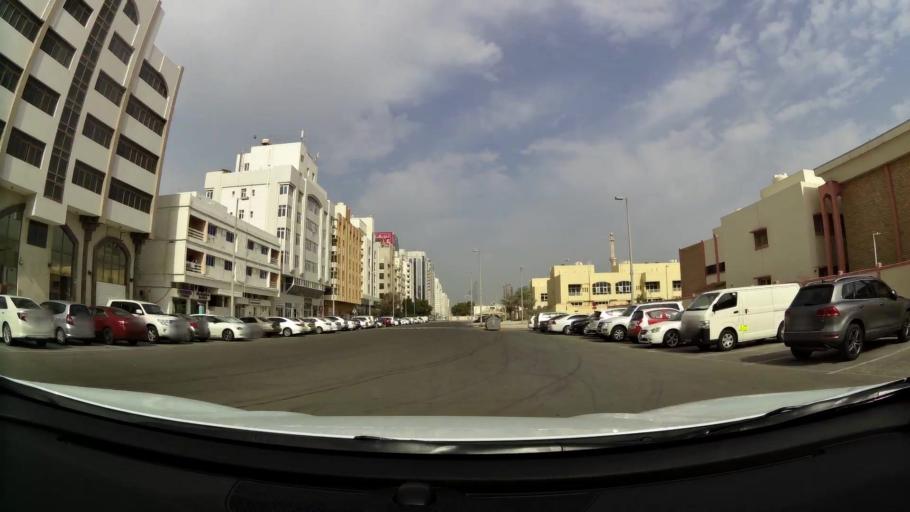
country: AE
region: Abu Dhabi
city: Abu Dhabi
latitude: 24.4568
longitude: 54.3846
